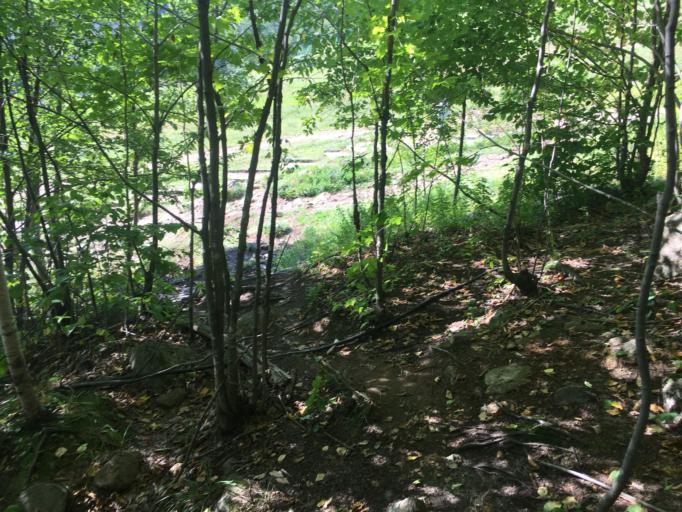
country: CA
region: Quebec
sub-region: Laurentides
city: Mont-Tremblant
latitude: 46.2138
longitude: -74.5822
